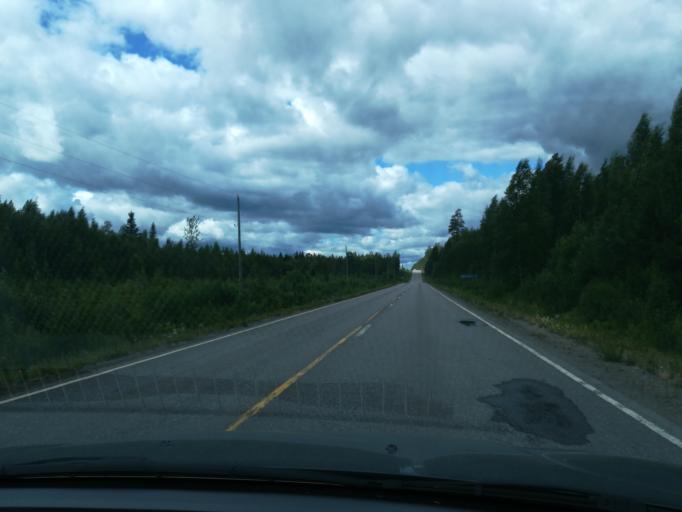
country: FI
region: Southern Savonia
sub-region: Mikkeli
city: Maentyharju
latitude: 61.3644
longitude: 26.9950
